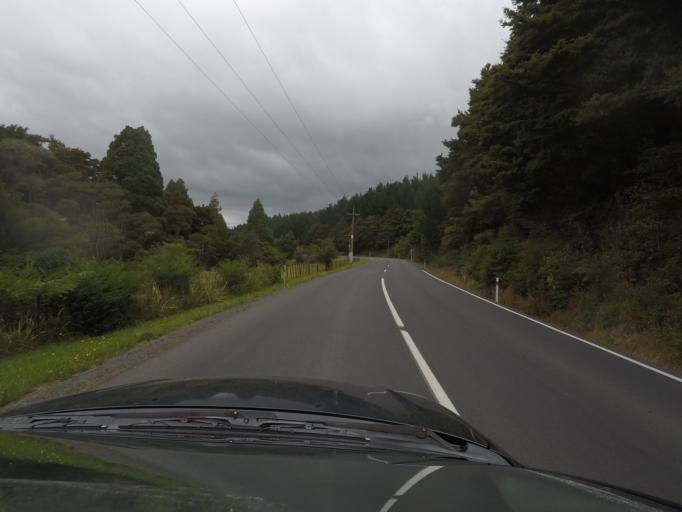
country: NZ
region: Auckland
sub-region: Auckland
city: Wellsford
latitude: -36.2863
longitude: 174.6131
